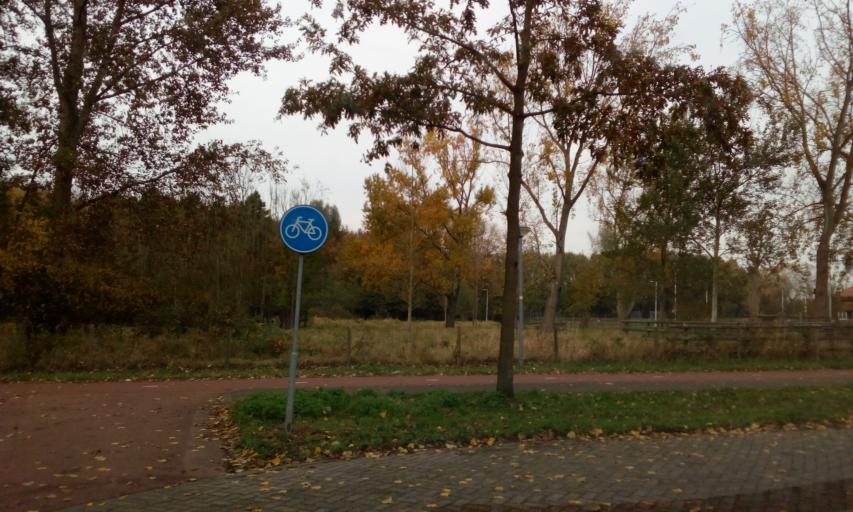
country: NL
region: South Holland
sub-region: Gemeente Lansingerland
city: Berkel en Rodenrijs
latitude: 51.9662
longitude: 4.4787
